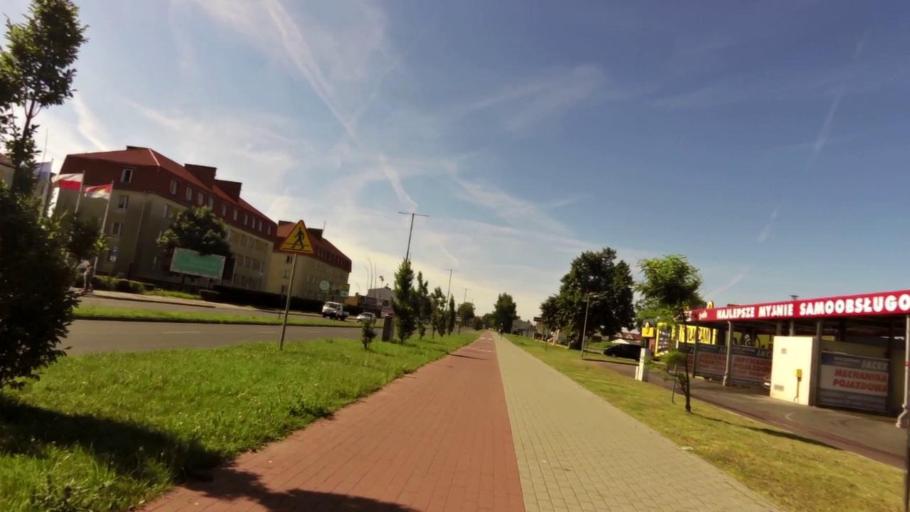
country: PL
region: West Pomeranian Voivodeship
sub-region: Powiat kolobrzeski
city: Kolobrzeg
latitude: 54.1702
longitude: 15.5707
